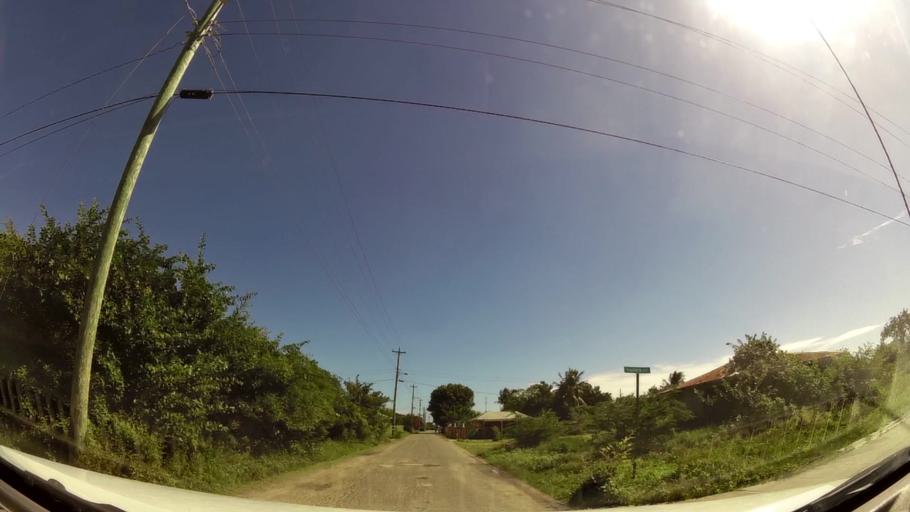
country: AG
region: Barbuda
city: Codrington
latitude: 17.6379
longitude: -61.8261
